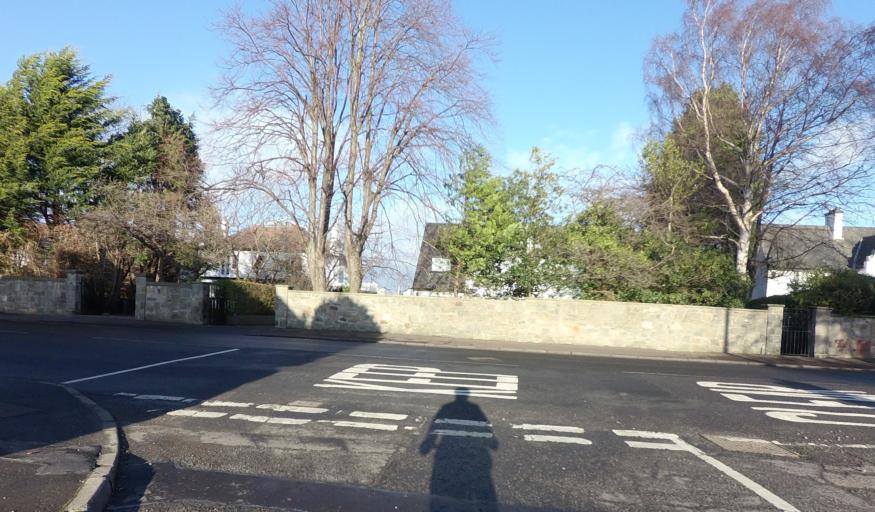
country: GB
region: Scotland
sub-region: Edinburgh
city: Currie
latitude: 55.9703
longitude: -3.3040
